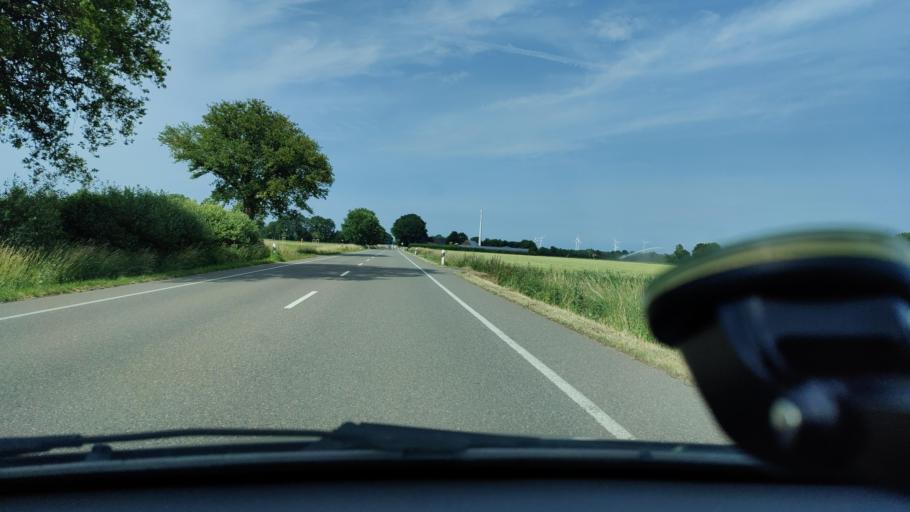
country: DE
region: North Rhine-Westphalia
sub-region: Regierungsbezirk Munster
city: Legden
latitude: 51.9810
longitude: 7.0998
